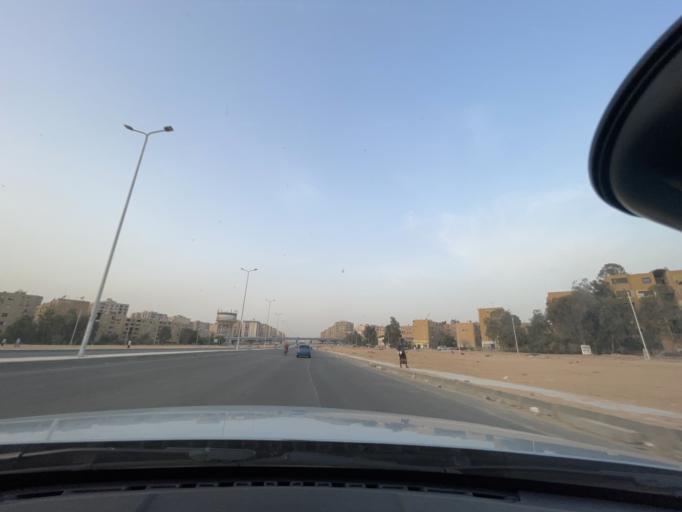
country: EG
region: Muhafazat al Qahirah
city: Cairo
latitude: 30.0445
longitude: 31.3631
